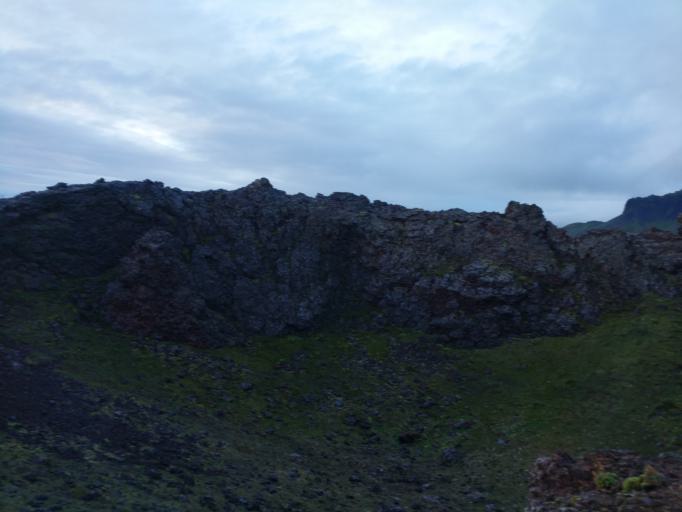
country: IS
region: West
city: Olafsvik
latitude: 64.8514
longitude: -23.9274
